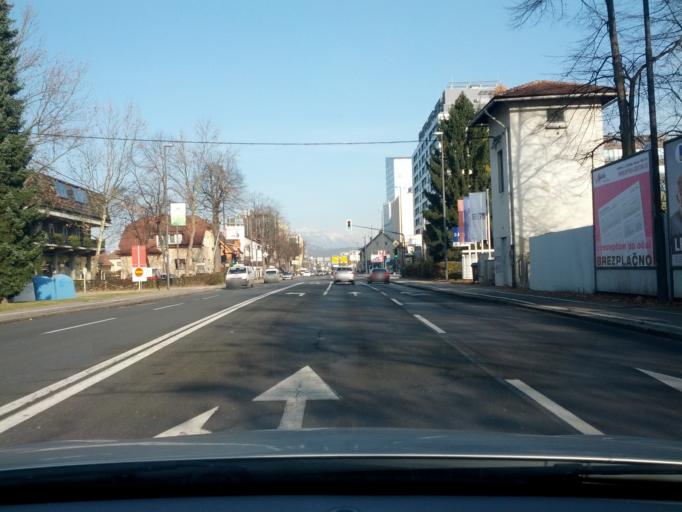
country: SI
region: Ljubljana
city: Ljubljana
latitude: 46.0786
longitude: 14.5123
